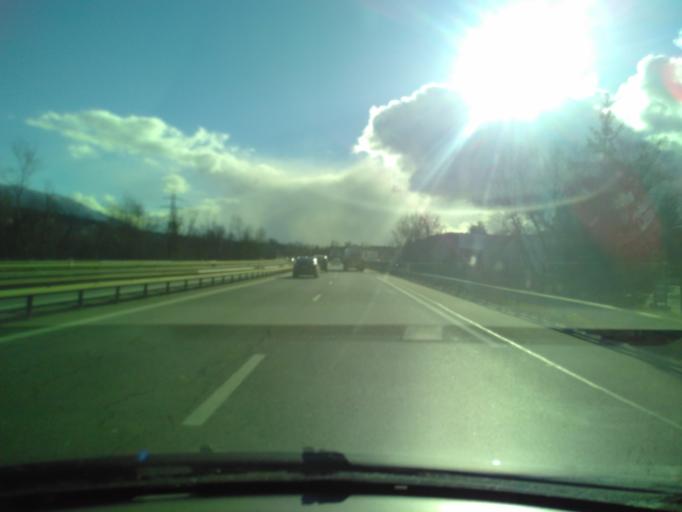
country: FR
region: Rhone-Alpes
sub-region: Departement de la Haute-Savoie
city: Meythet
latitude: 45.9148
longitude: 6.0982
